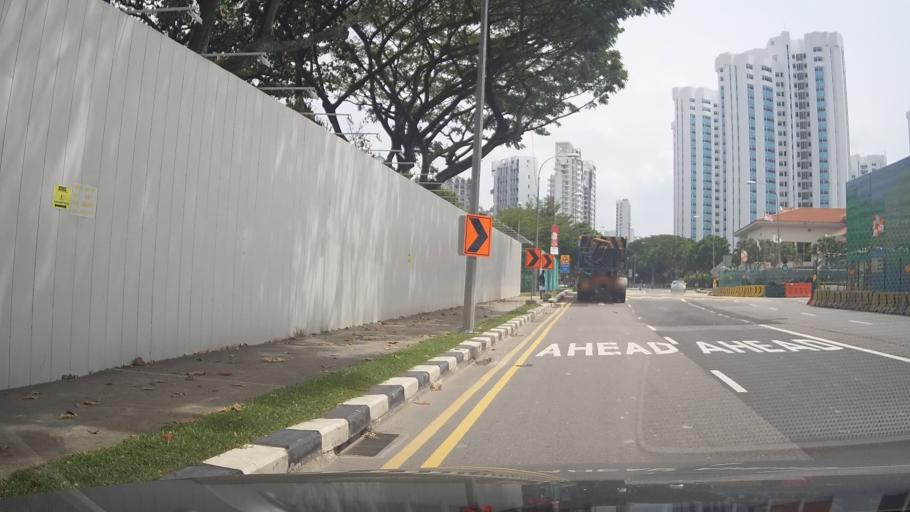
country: SG
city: Singapore
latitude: 1.2978
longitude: 103.8800
